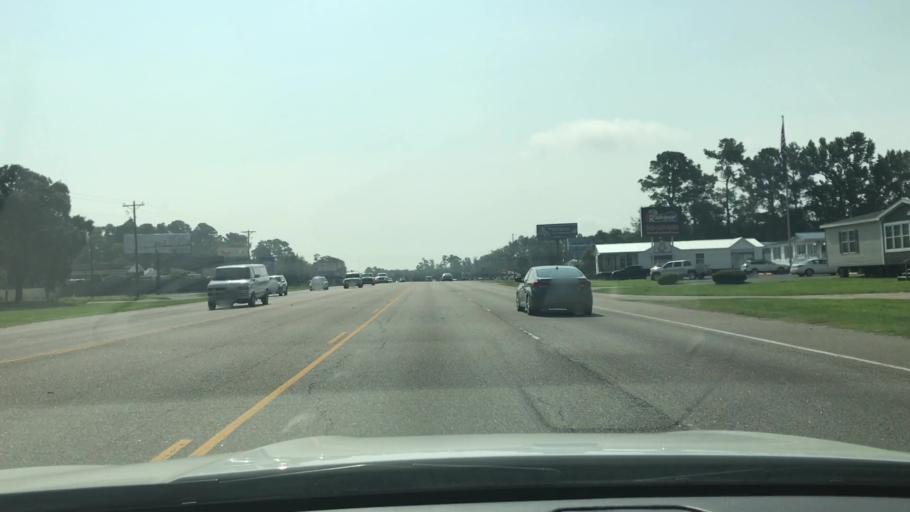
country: US
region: South Carolina
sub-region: Horry County
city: Red Hill
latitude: 33.8128
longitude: -79.0288
